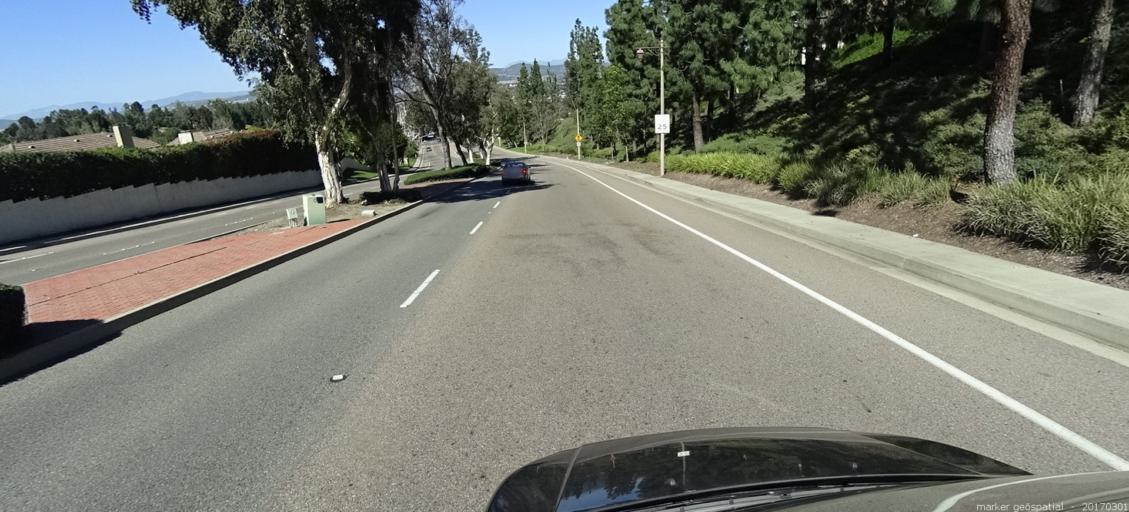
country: US
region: California
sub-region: Orange County
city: Villa Park
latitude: 33.8411
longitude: -117.7906
